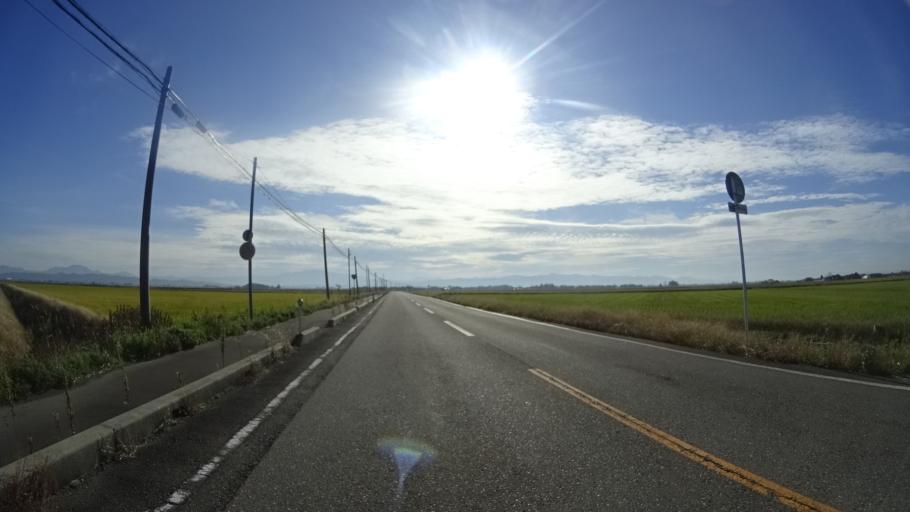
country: JP
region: Niigata
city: Mitsuke
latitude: 37.5690
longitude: 138.8427
